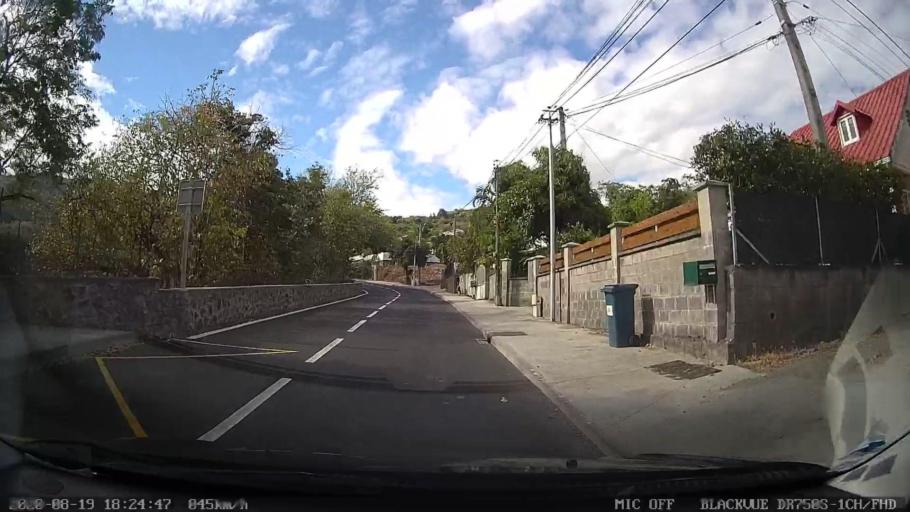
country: RE
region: Reunion
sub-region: Reunion
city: La Possession
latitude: -20.9524
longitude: 55.3472
